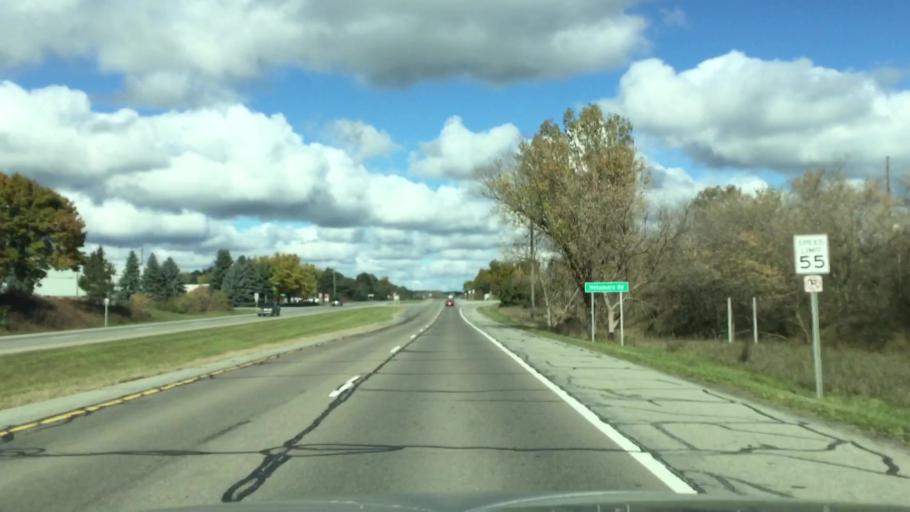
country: US
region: Michigan
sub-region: Oakland County
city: Oxford
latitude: 42.8593
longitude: -83.2880
